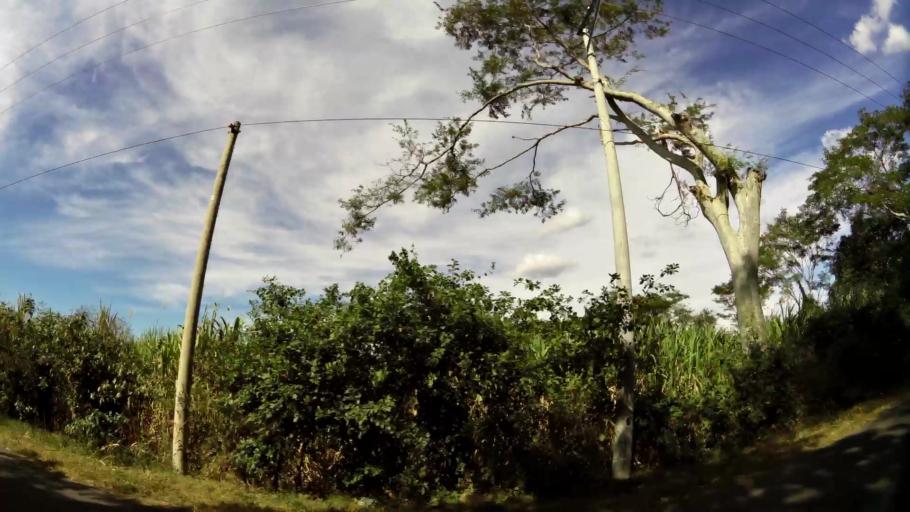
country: SV
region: San Salvador
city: Aguilares
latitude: 13.9586
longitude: -89.1528
